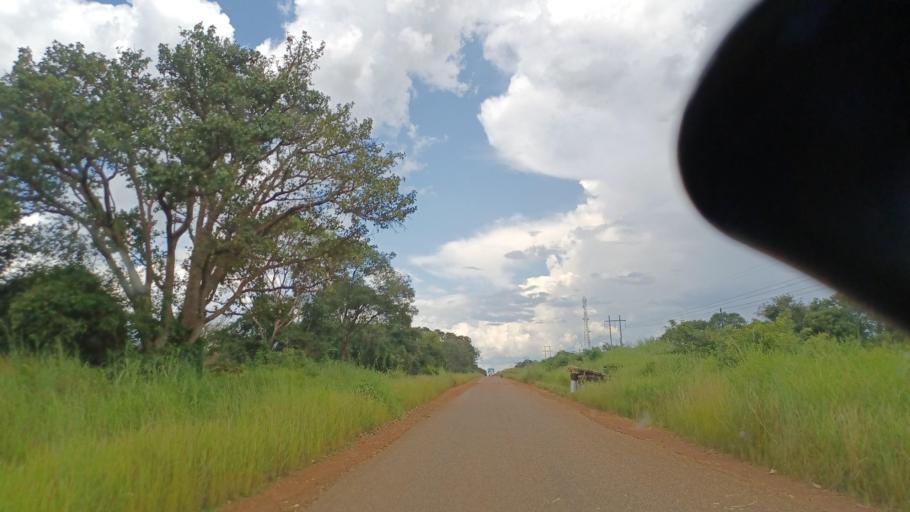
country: ZM
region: North-Western
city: Kasempa
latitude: -12.7919
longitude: 26.0144
